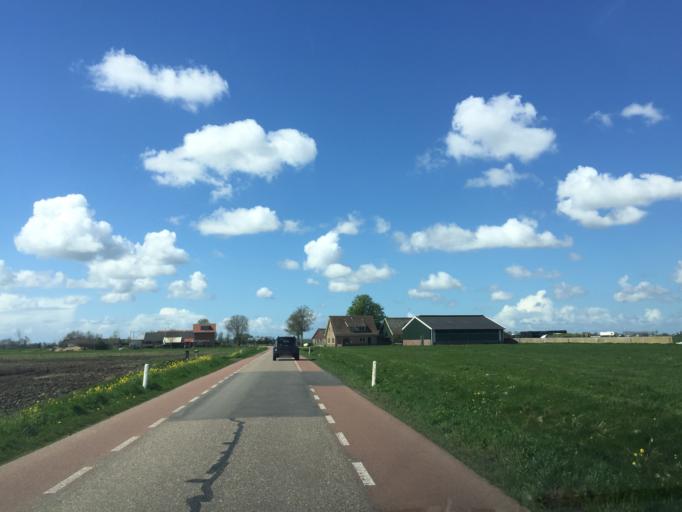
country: NL
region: South Holland
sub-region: Gemeente Kaag en Braassem
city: Leimuiden
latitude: 52.2080
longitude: 4.6975
